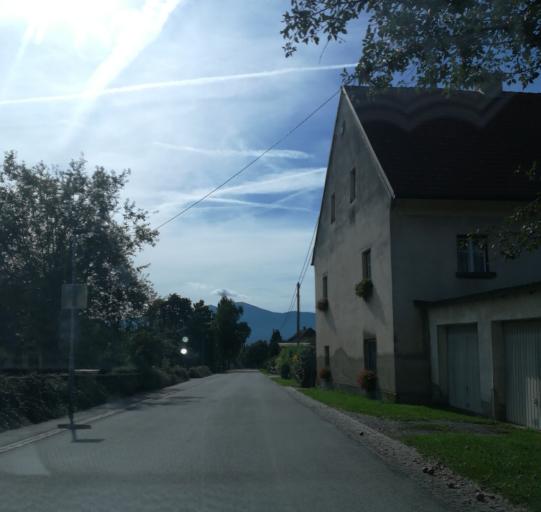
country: AT
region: Styria
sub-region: Politischer Bezirk Murtal
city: Flatschach
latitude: 47.2174
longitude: 14.7533
